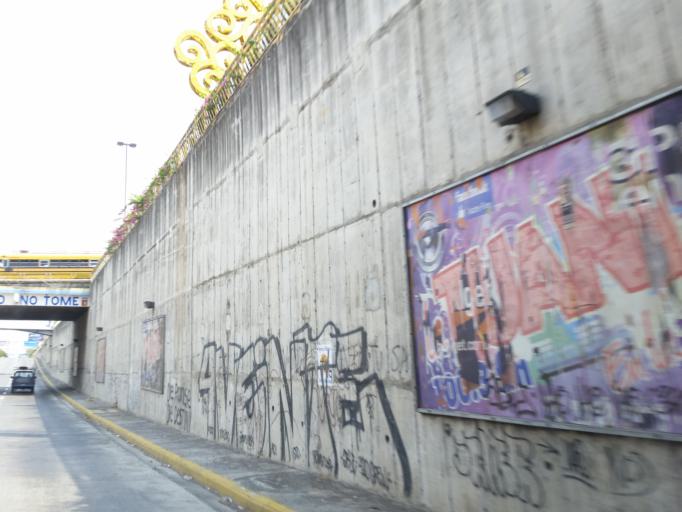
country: NI
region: Managua
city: Managua
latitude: 12.1133
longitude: -86.2552
